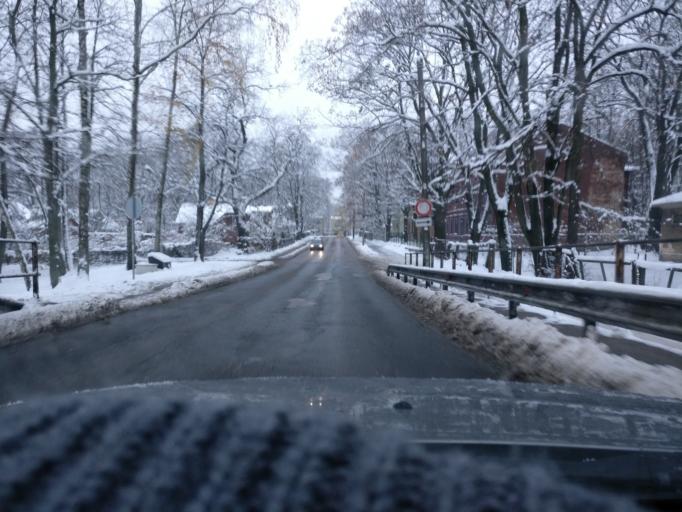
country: LV
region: Riga
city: Riga
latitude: 56.9286
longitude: 24.0841
